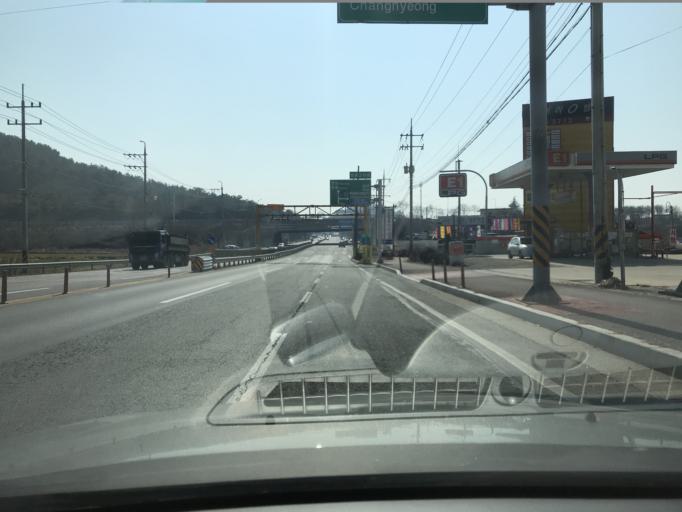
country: KR
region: Daegu
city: Hwawon
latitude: 35.7074
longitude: 128.4369
